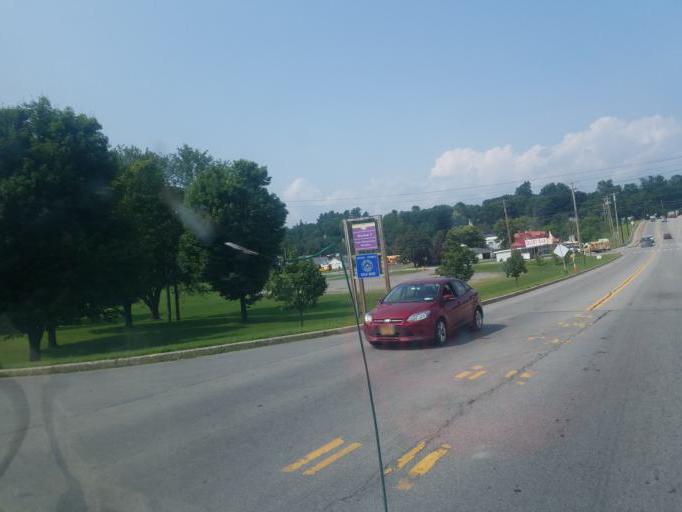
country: US
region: New York
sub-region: Montgomery County
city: Fonda
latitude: 42.9515
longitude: -74.3695
